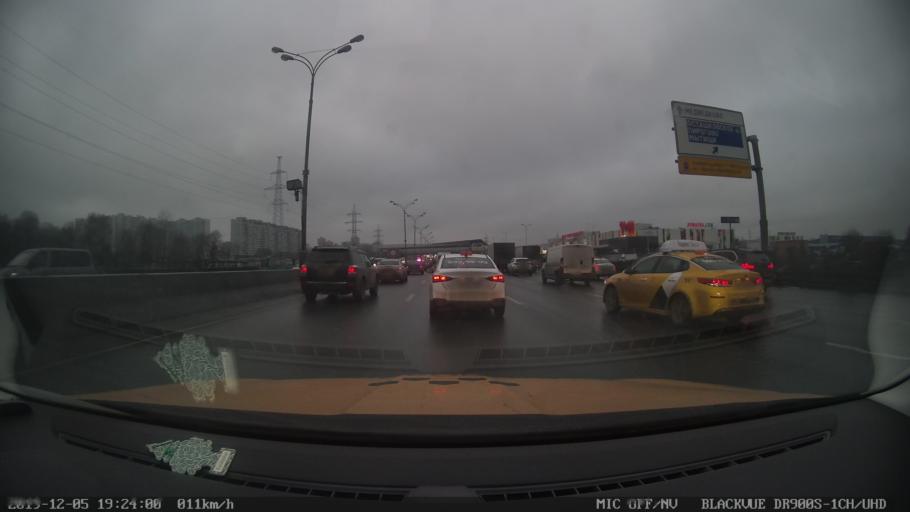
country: RU
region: Moscow
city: Vatutino
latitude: 55.8945
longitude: 37.6875
